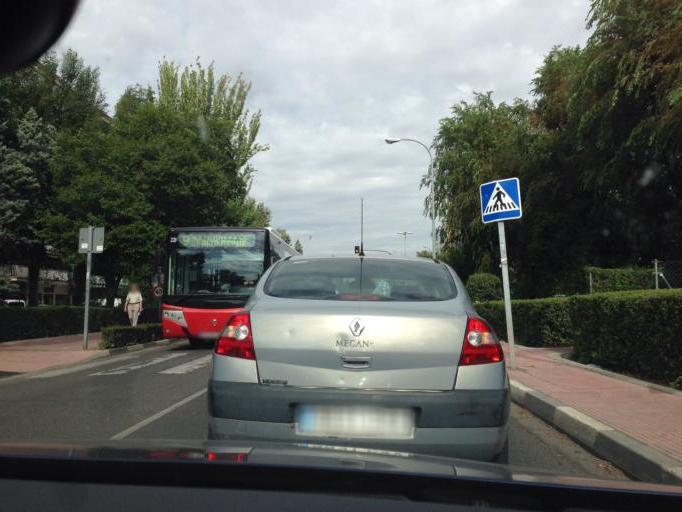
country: ES
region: Madrid
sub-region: Provincia de Madrid
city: Alcala de Henares
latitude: 40.4909
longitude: -3.3768
